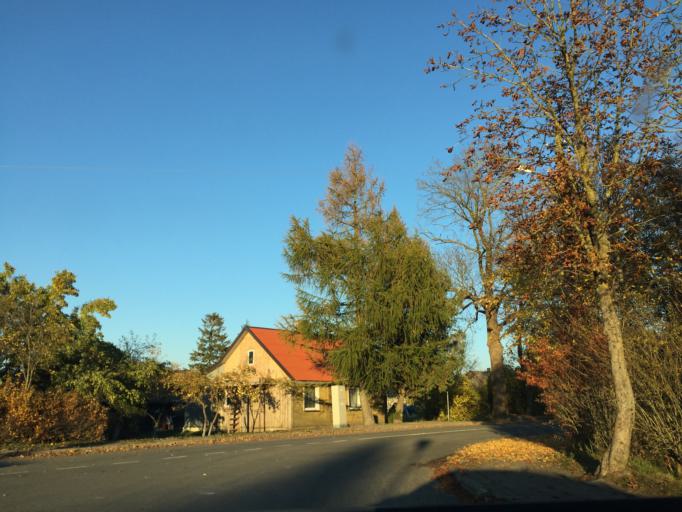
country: LT
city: Vieksniai
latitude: 56.3814
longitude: 22.5574
